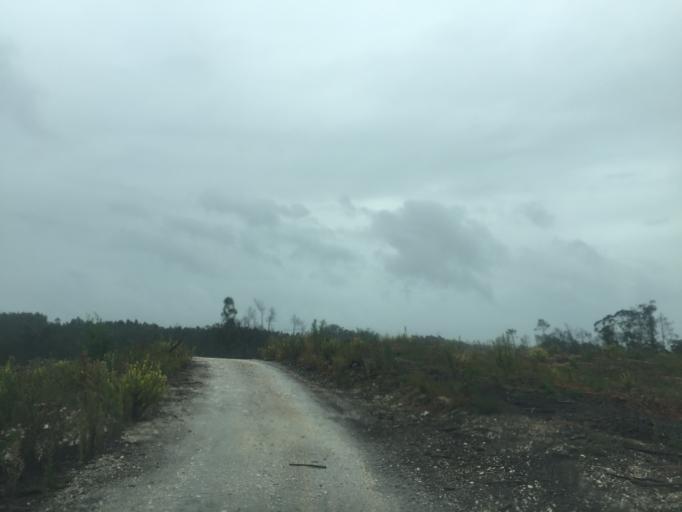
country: PT
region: Coimbra
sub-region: Figueira da Foz
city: Lavos
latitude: 40.0720
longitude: -8.7857
